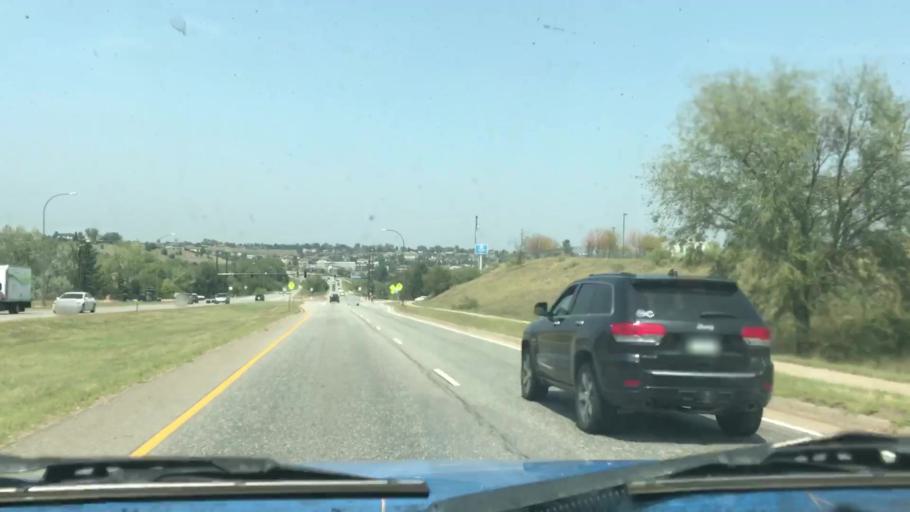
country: US
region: Colorado
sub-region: Jefferson County
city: Lakewood
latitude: 39.6587
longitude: -105.1120
